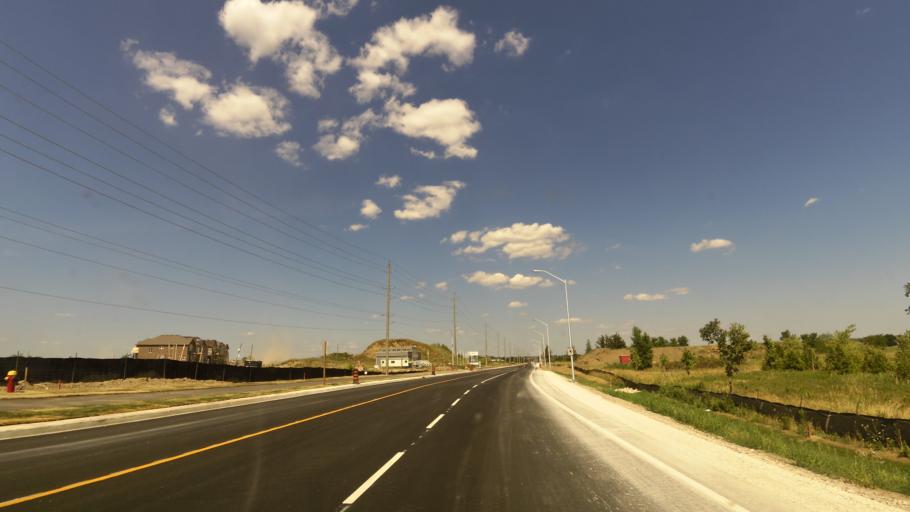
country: CA
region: Ontario
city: Brampton
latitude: 43.6330
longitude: -79.8680
